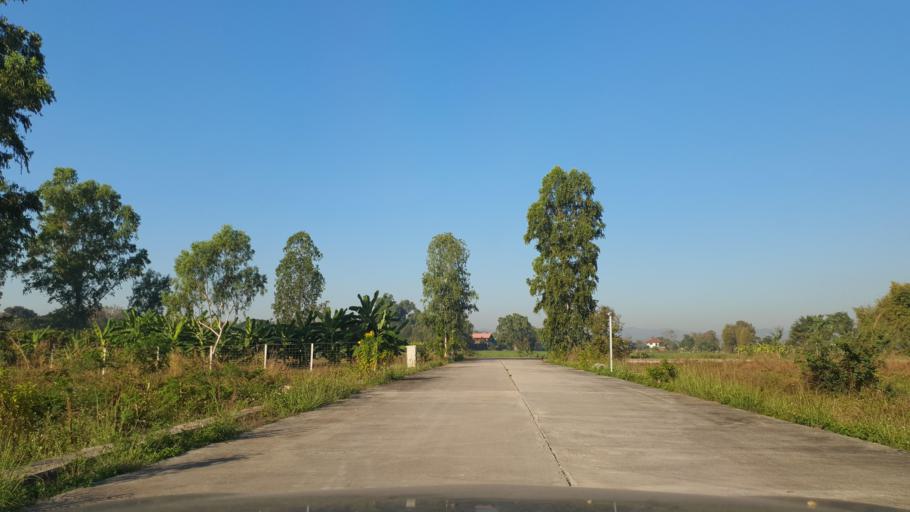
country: TH
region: Chiang Mai
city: Hang Dong
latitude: 18.6937
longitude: 98.9690
